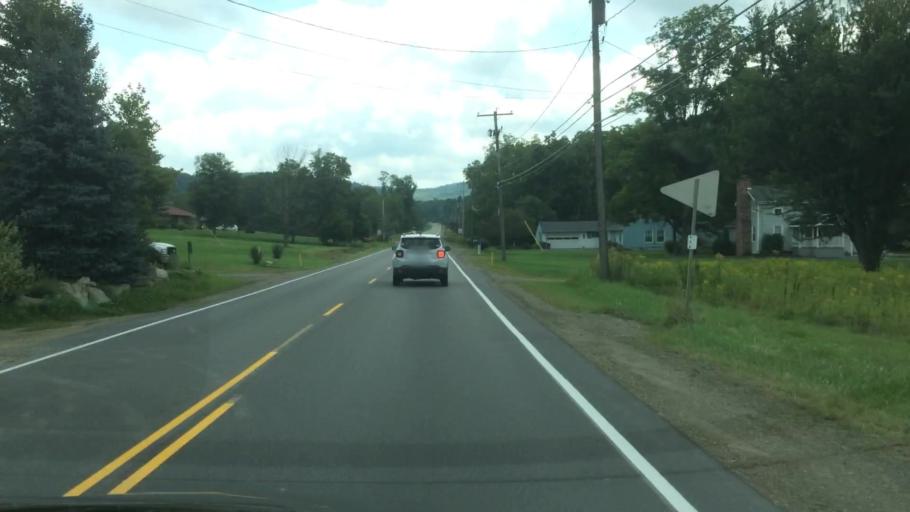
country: US
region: Pennsylvania
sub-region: McKean County
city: Bradford
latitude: 41.9008
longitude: -78.6108
